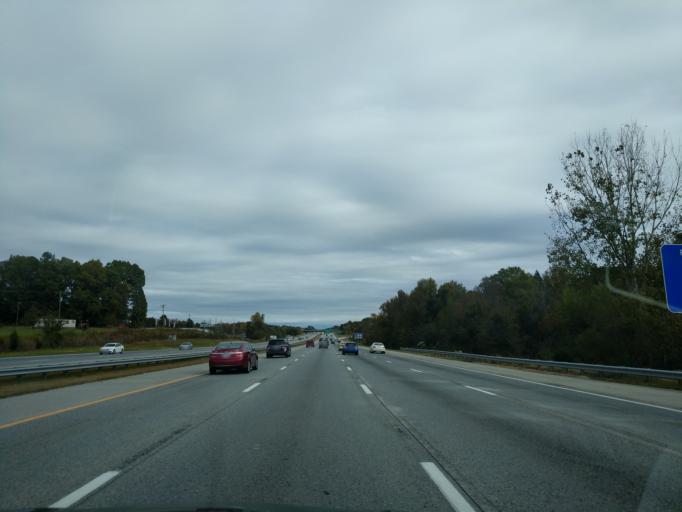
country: US
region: North Carolina
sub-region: Rowan County
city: Salisbury
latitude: 35.6274
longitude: -80.4983
